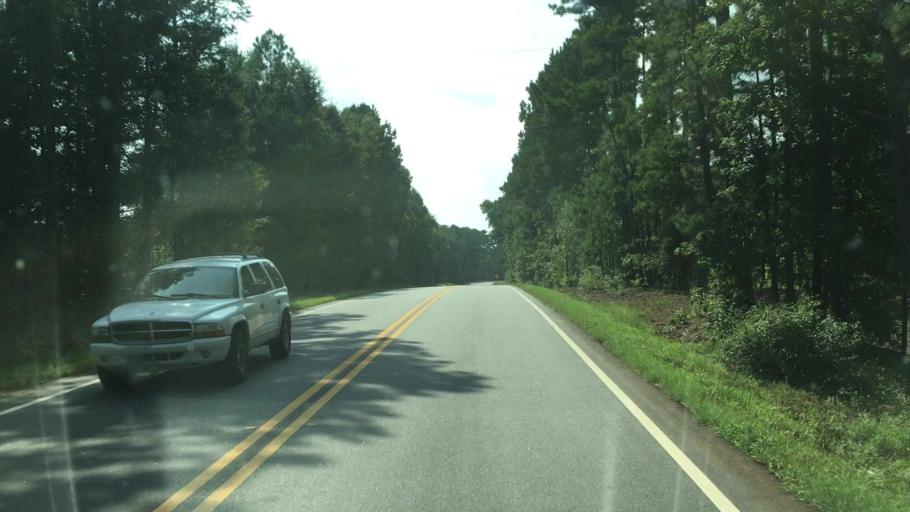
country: US
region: Georgia
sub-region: Jasper County
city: Monticello
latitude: 33.3554
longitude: -83.7434
